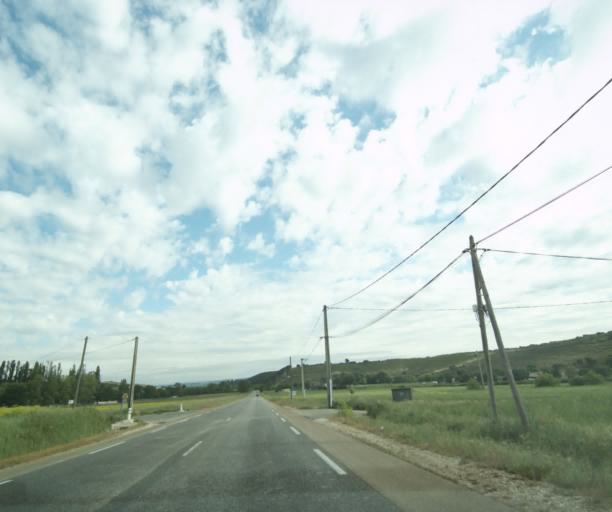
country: FR
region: Provence-Alpes-Cote d'Azur
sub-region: Departement des Bouches-du-Rhone
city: Cabries
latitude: 43.4718
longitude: 5.3548
